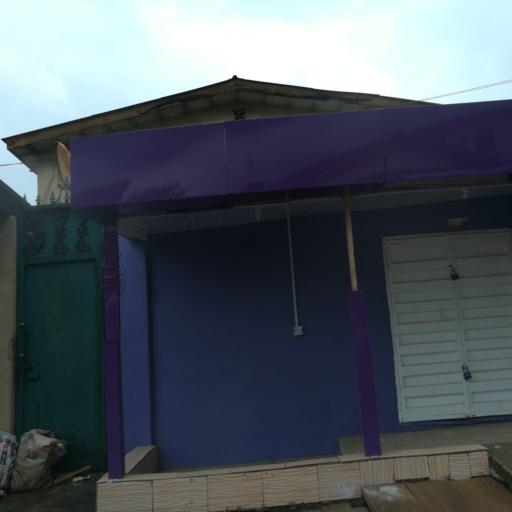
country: NG
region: Lagos
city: Agege
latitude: 6.5966
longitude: 3.2948
